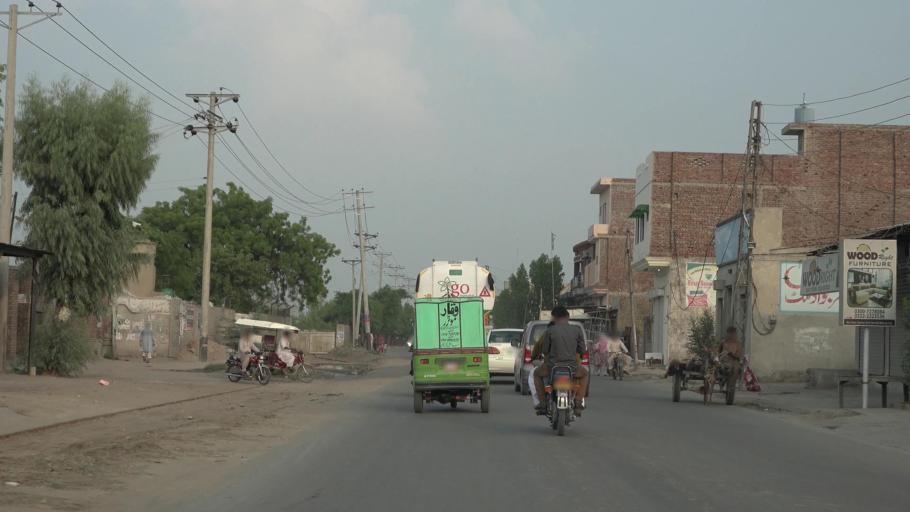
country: PK
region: Punjab
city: Faisalabad
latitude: 31.4488
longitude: 73.1244
